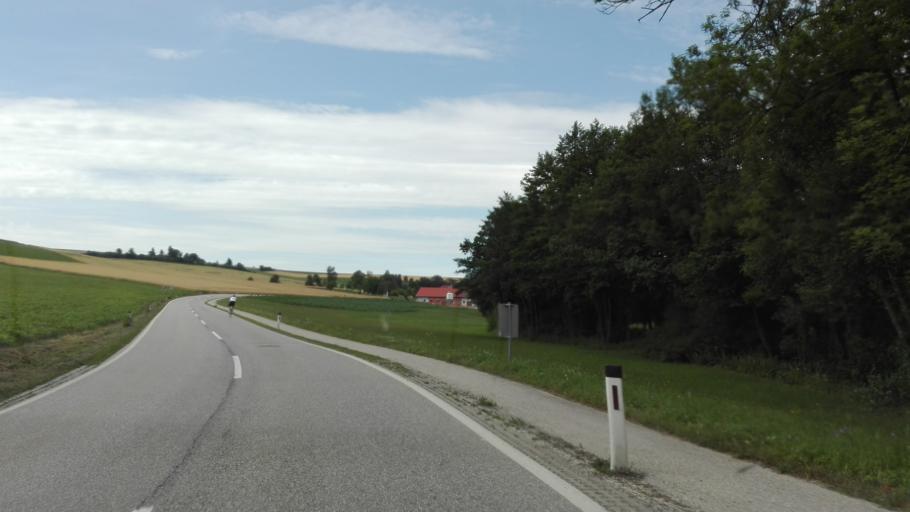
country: AT
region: Upper Austria
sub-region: Politischer Bezirk Grieskirchen
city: Grieskirchen
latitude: 48.2507
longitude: 13.8133
